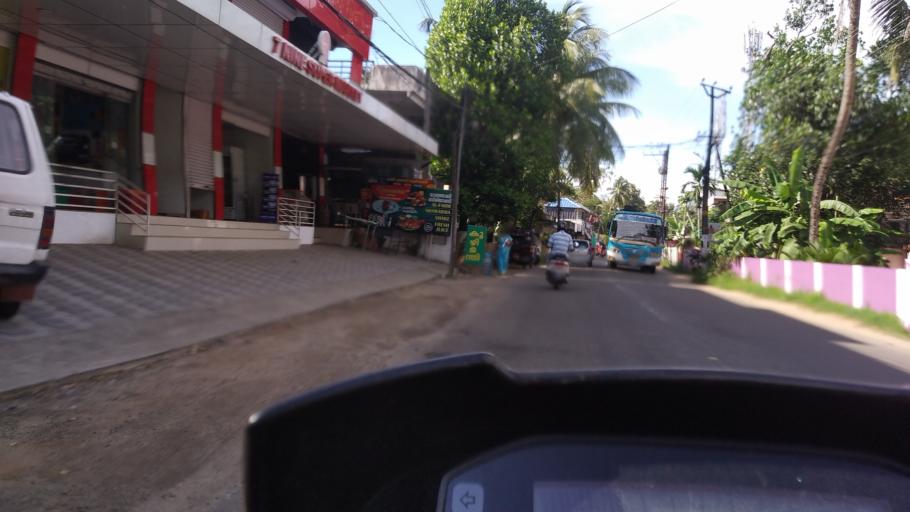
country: IN
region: Kerala
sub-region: Ernakulam
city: Elur
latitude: 10.0623
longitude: 76.2134
